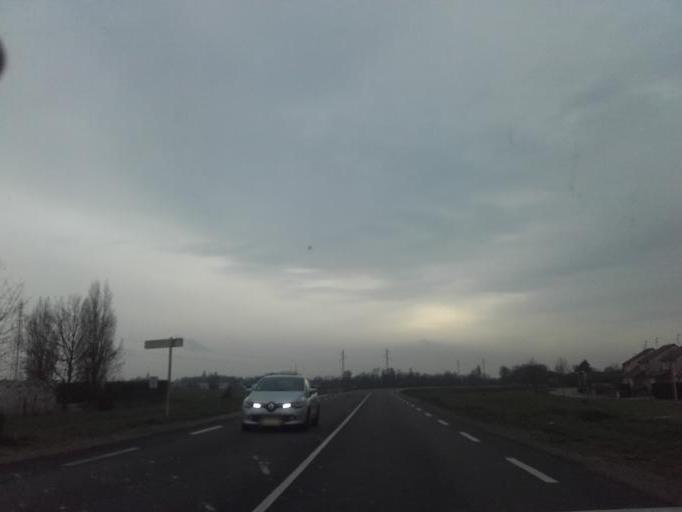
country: FR
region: Bourgogne
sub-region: Departement de la Cote-d'Or
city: Beaune
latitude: 47.0160
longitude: 4.8563
